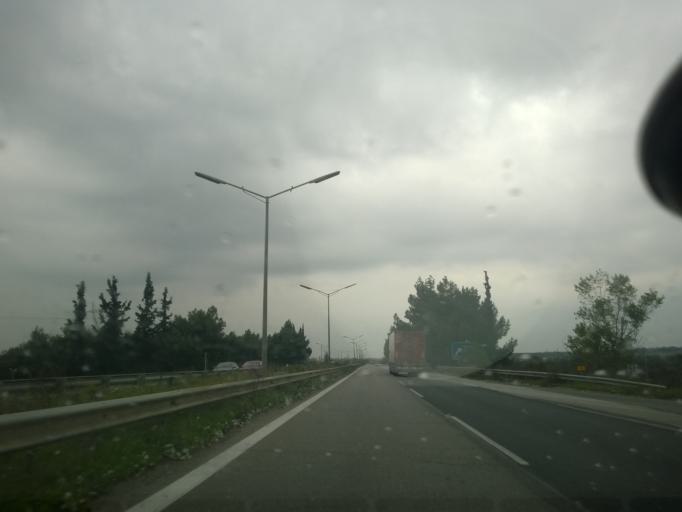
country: GR
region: Central Macedonia
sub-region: Nomos Thessalonikis
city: Agios Athanasios
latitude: 40.7228
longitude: 22.7164
